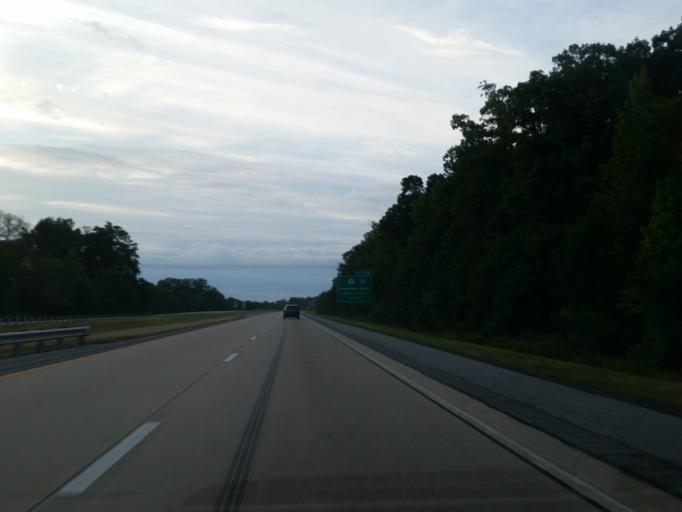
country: US
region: Delaware
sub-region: Kent County
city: Dover
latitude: 39.1764
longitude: -75.5024
